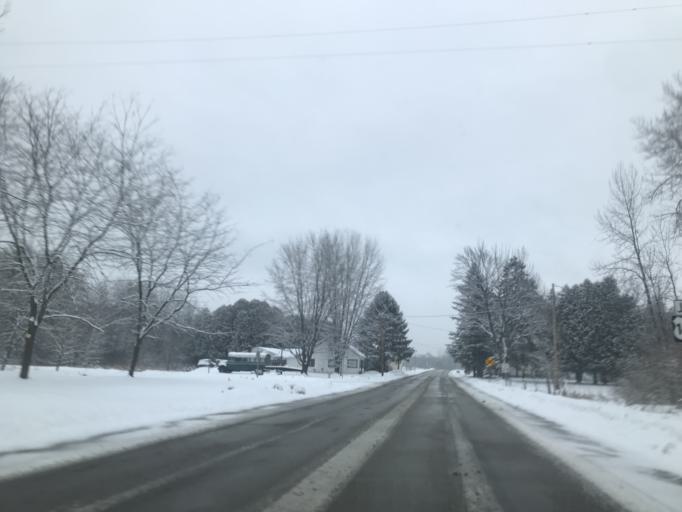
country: US
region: Wisconsin
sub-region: Oconto County
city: Oconto Falls
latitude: 44.8617
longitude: -88.0527
